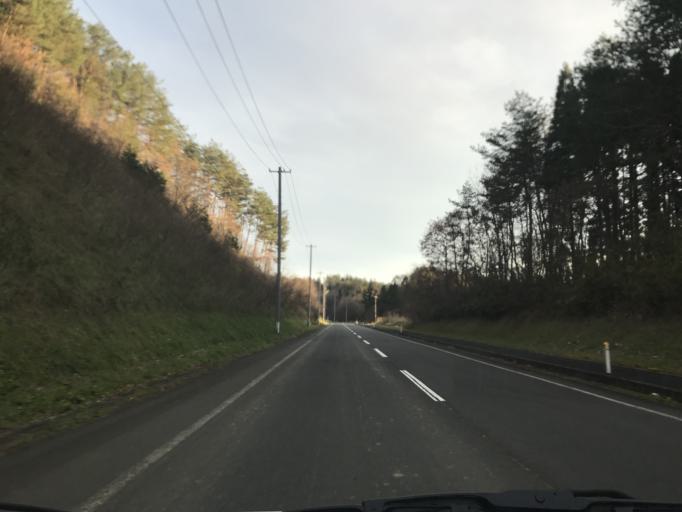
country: JP
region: Iwate
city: Ichinoseki
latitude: 38.9891
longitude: 141.0670
